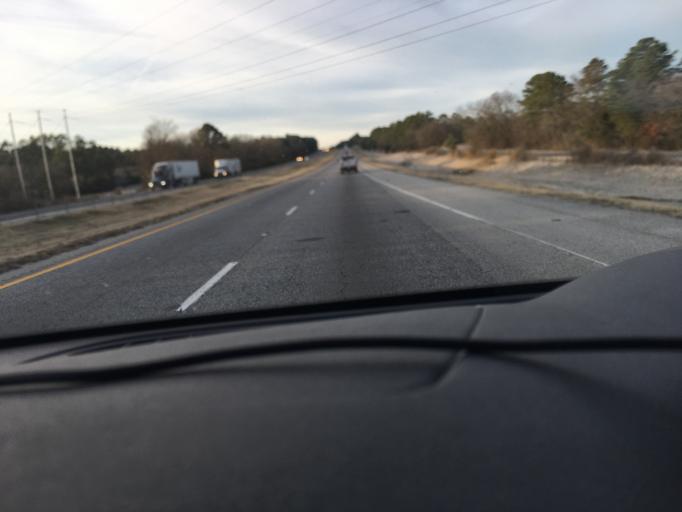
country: US
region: Arkansas
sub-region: Hot Spring County
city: Malvern
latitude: 34.3288
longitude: -92.9241
